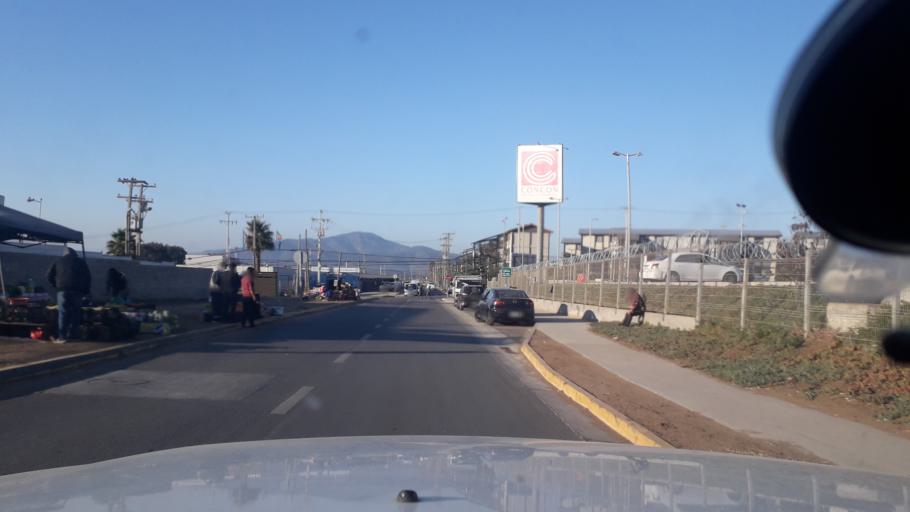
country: CL
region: Valparaiso
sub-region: Provincia de Valparaiso
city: Vina del Mar
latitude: -32.9311
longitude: -71.5188
